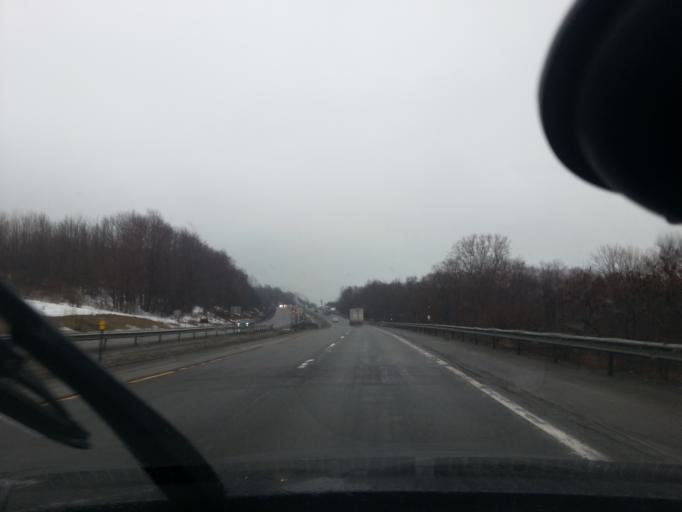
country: US
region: New York
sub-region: Onondaga County
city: Nedrow
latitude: 42.8536
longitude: -76.1200
